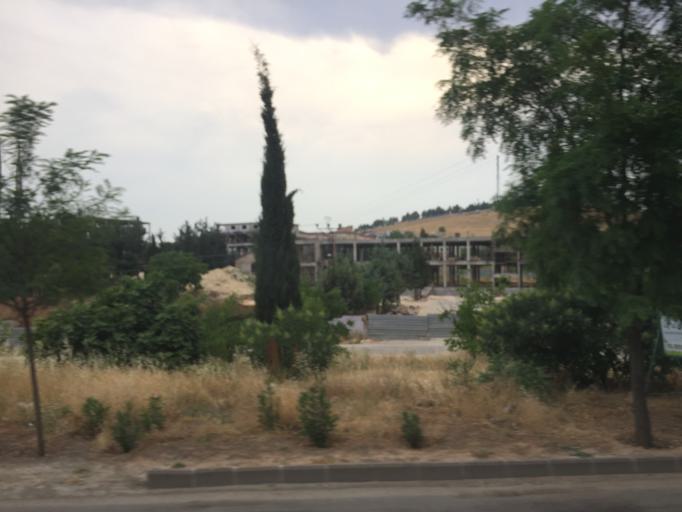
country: TR
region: Gaziantep
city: Gaziantep
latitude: 37.0117
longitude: 37.4304
